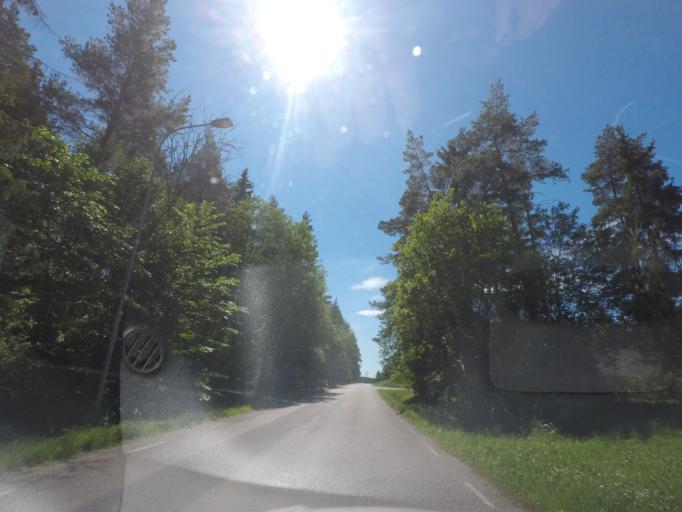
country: SE
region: Uppsala
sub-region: Enkopings Kommun
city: Irsta
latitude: 59.6742
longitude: 16.8382
